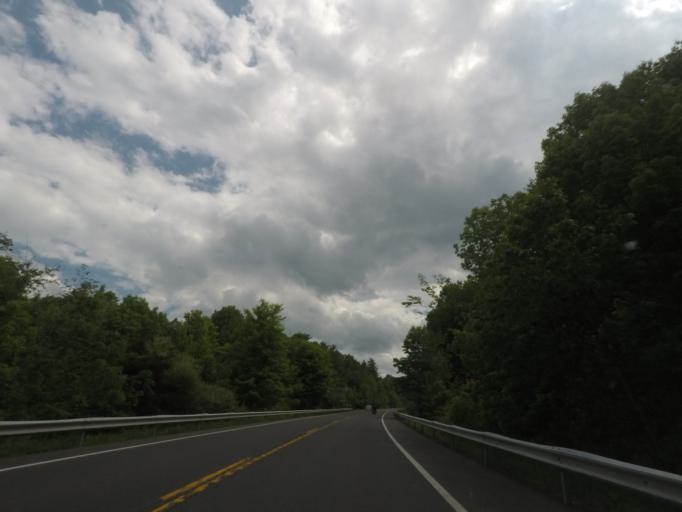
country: US
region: New York
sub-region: Dutchess County
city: Pine Plains
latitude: 42.0979
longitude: -73.6891
